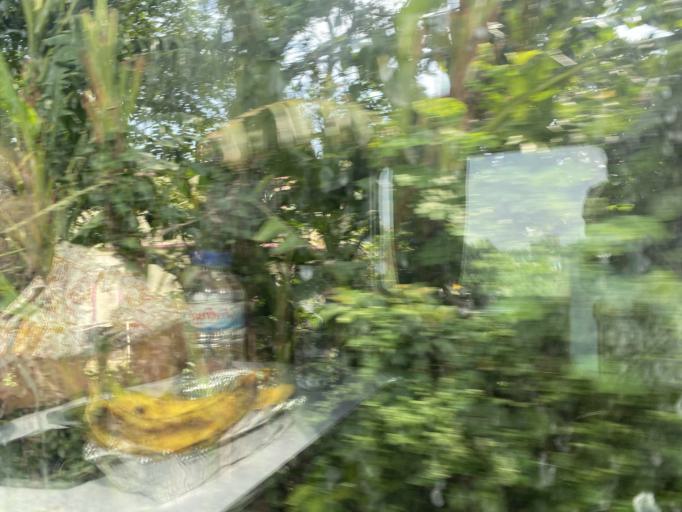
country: BD
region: Chittagong
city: Nabinagar
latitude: 23.9493
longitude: 91.1200
